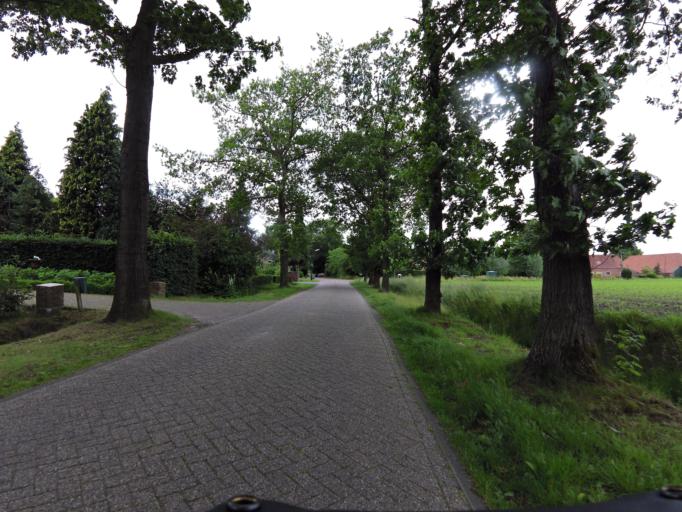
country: NL
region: North Brabant
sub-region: Gemeente Baarle-Nassau
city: Baarle-Nassau
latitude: 51.4760
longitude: 4.9405
